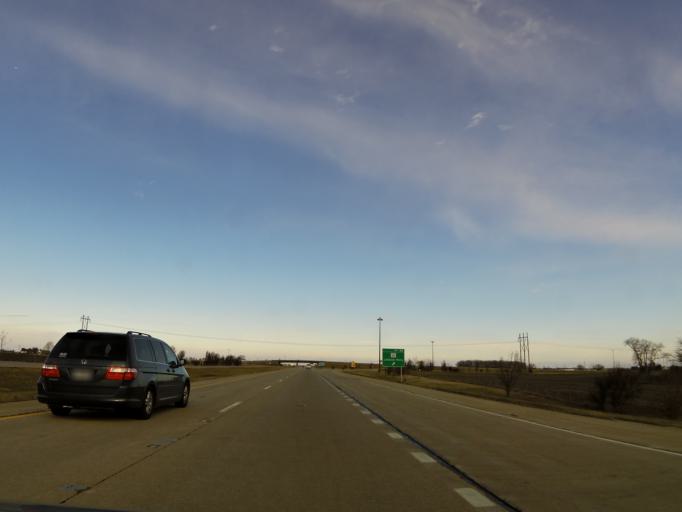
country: US
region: Illinois
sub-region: LaSalle County
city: Oglesby
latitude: 41.2698
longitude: -89.0813
